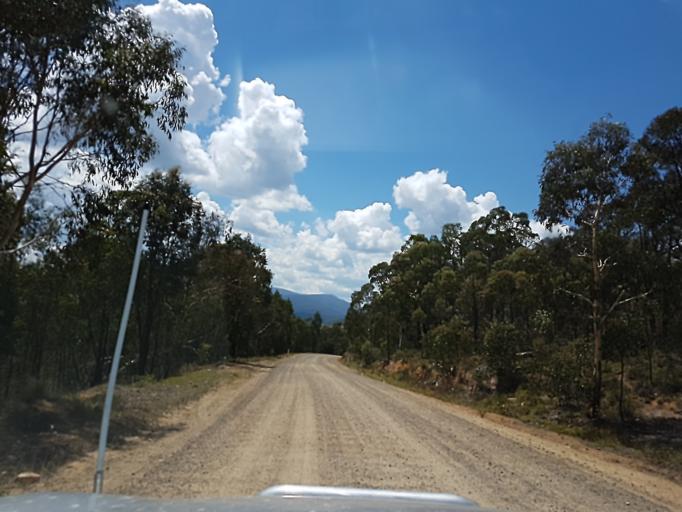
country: AU
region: Victoria
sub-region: Alpine
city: Mount Beauty
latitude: -36.9004
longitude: 147.8152
